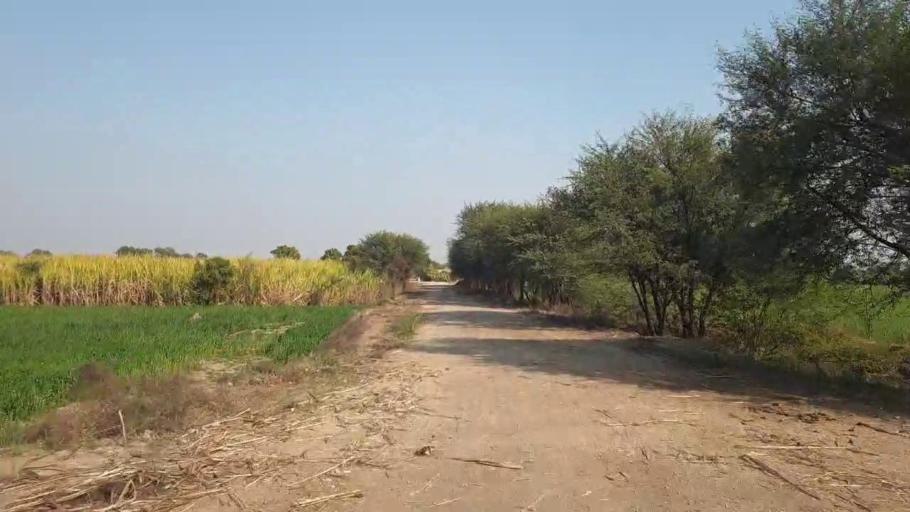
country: PK
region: Sindh
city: Mirwah Gorchani
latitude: 25.3881
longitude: 68.9540
